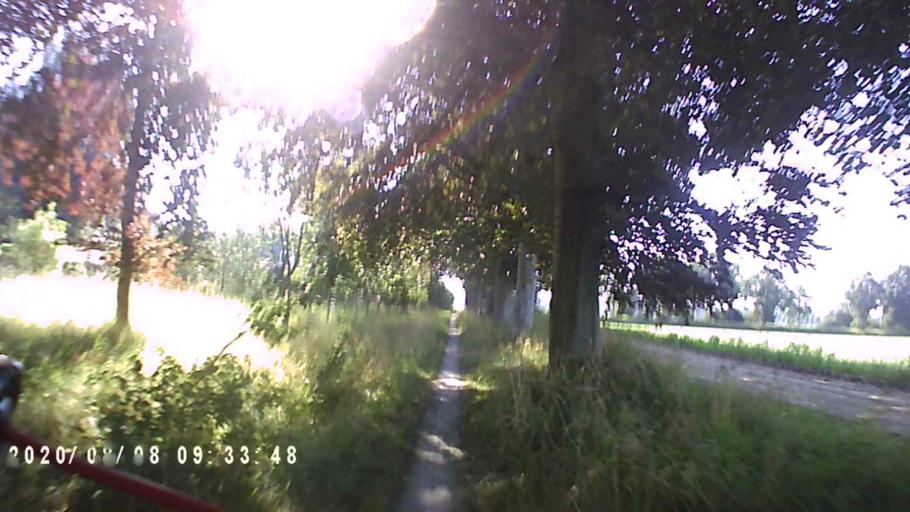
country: NL
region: Groningen
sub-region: Gemeente Leek
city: Leek
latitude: 53.0444
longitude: 6.3785
